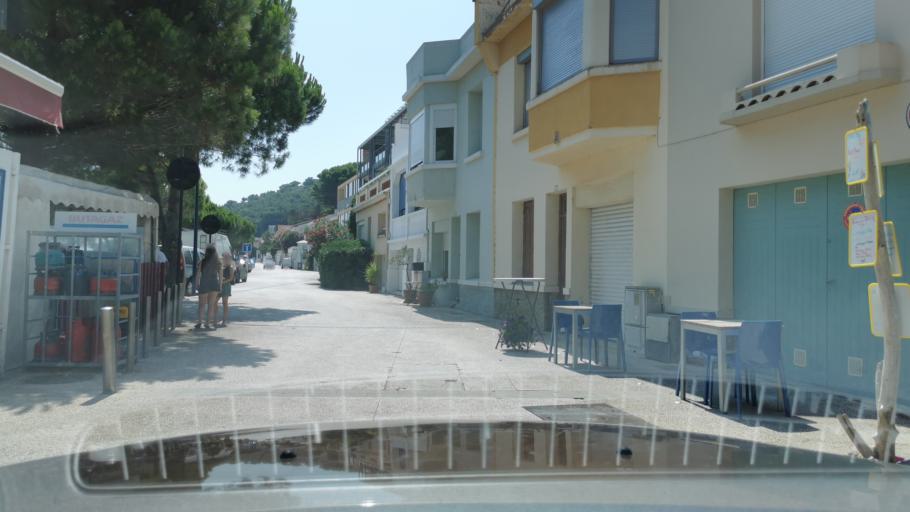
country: FR
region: Languedoc-Roussillon
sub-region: Departement de l'Aude
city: Leucate
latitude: 42.9309
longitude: 3.0380
